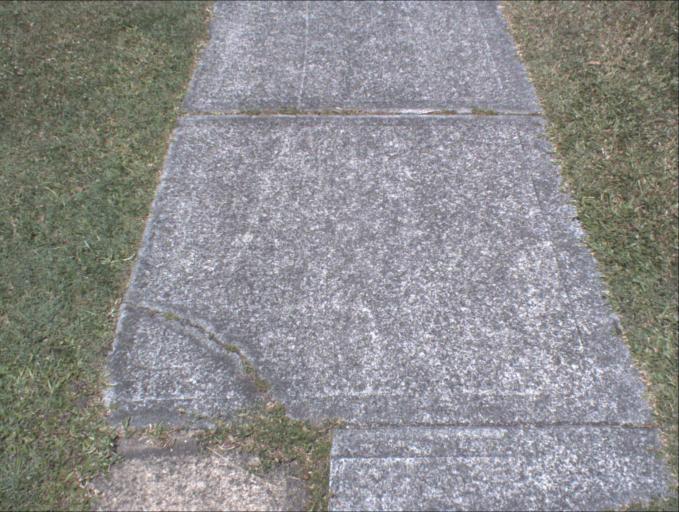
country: AU
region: Queensland
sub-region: Logan
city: Windaroo
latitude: -27.7340
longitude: 153.2068
